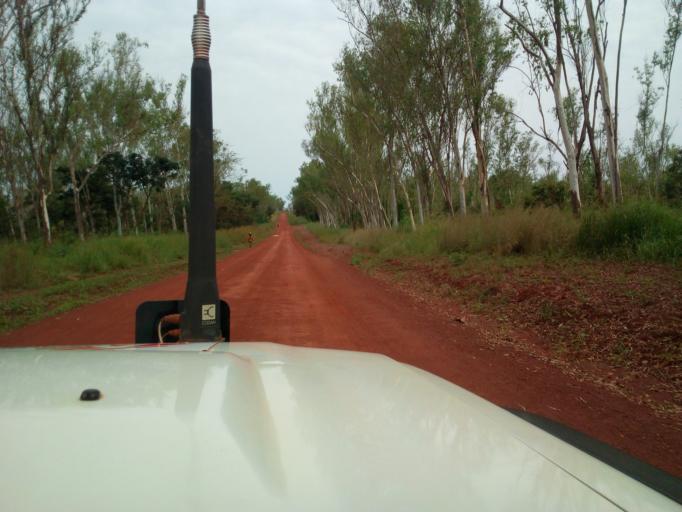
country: CF
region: Ouaka
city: Bambari
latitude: 5.7910
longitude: 20.6429
